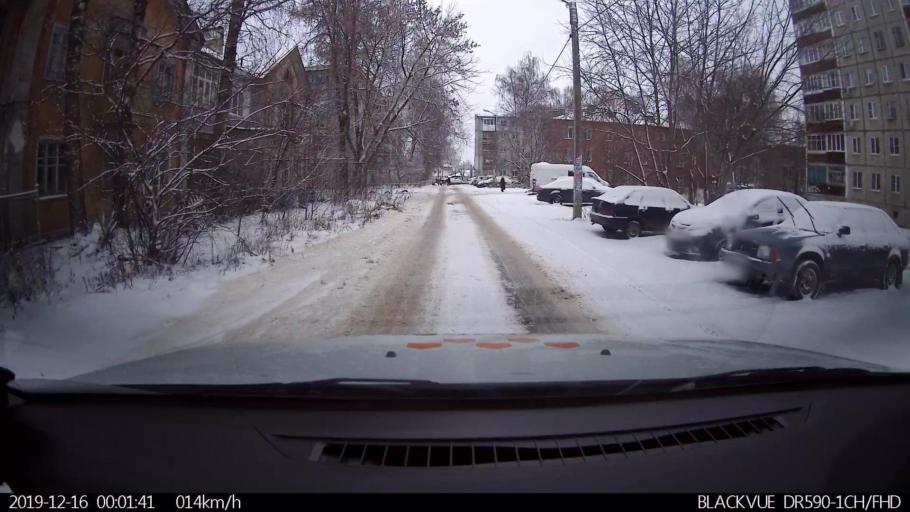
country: RU
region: Nizjnij Novgorod
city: Gorbatovka
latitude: 56.3583
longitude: 43.8441
